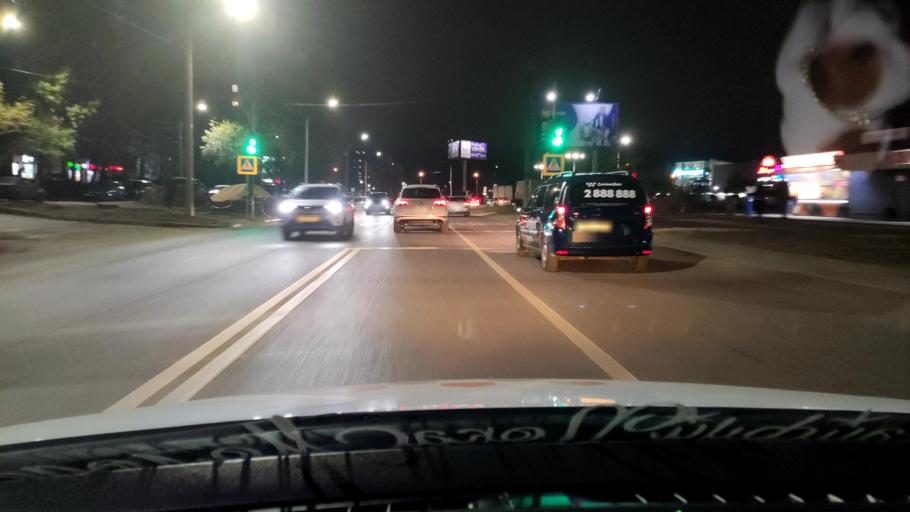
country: RU
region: Voronezj
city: Podgornoye
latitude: 51.7141
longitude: 39.1619
